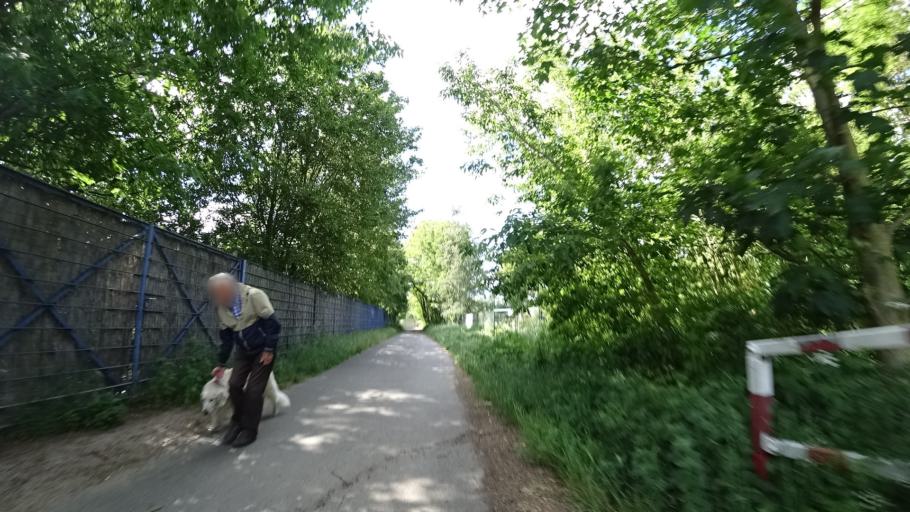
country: DE
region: Berlin
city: Lichtenrade
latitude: 52.3908
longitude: 13.3809
